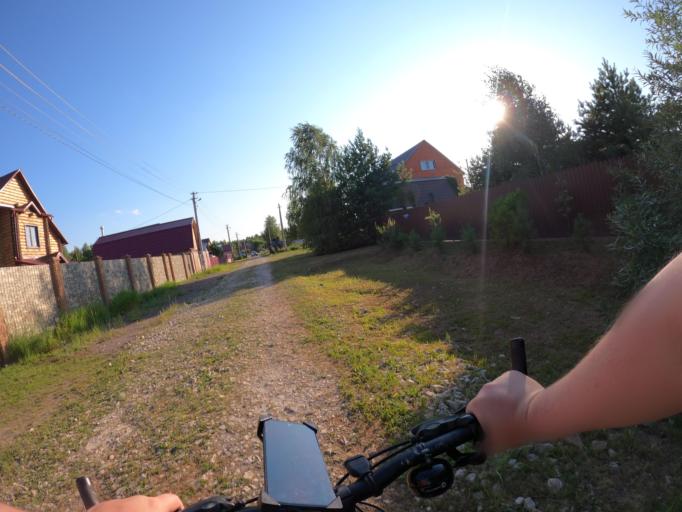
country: RU
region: Moskovskaya
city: Beloozerskiy
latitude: 55.4907
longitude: 38.4365
